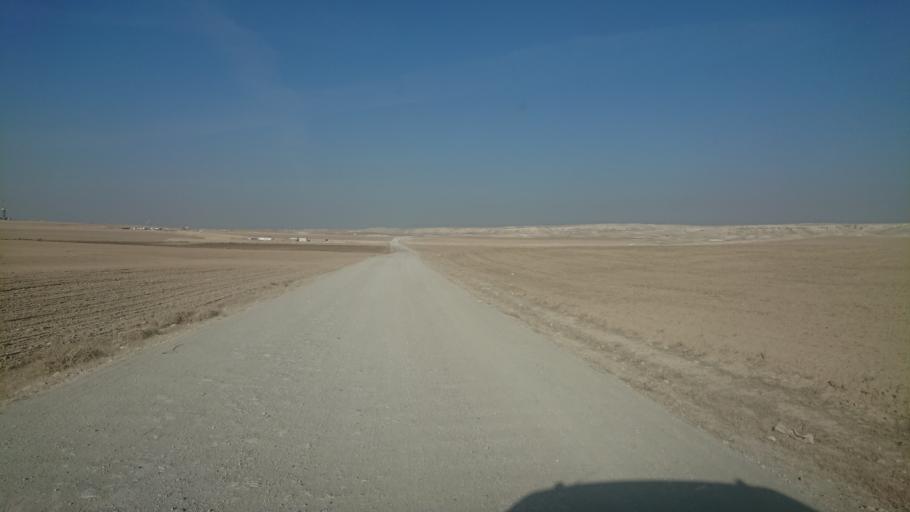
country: TR
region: Aksaray
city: Sultanhani
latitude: 38.0636
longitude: 33.6152
